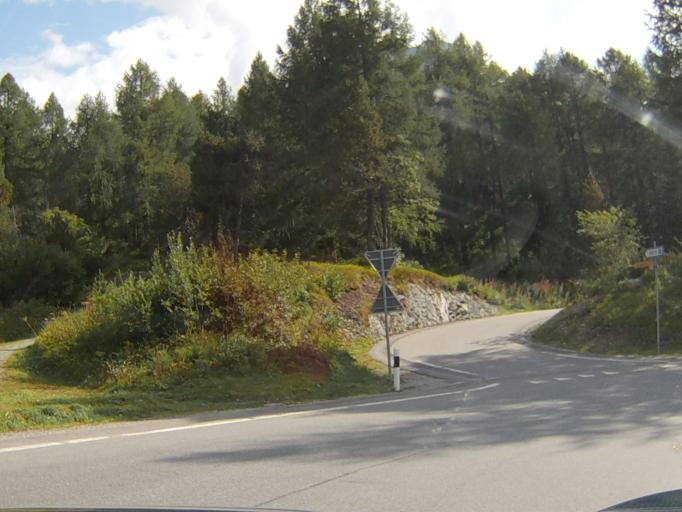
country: CH
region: Grisons
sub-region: Maloja District
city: Silvaplana
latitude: 46.3960
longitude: 9.6948
